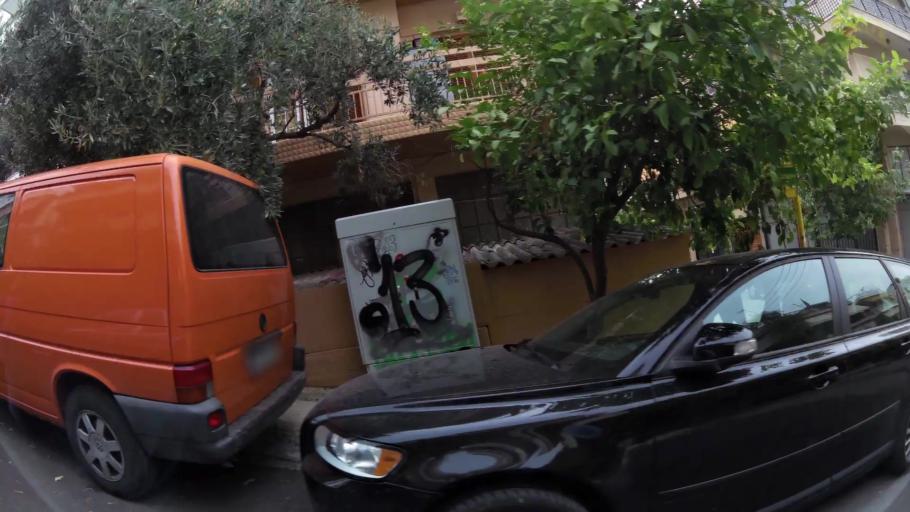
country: GR
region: Attica
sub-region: Nomarchia Athinas
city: Agios Dimitrios
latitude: 37.9222
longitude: 23.7334
